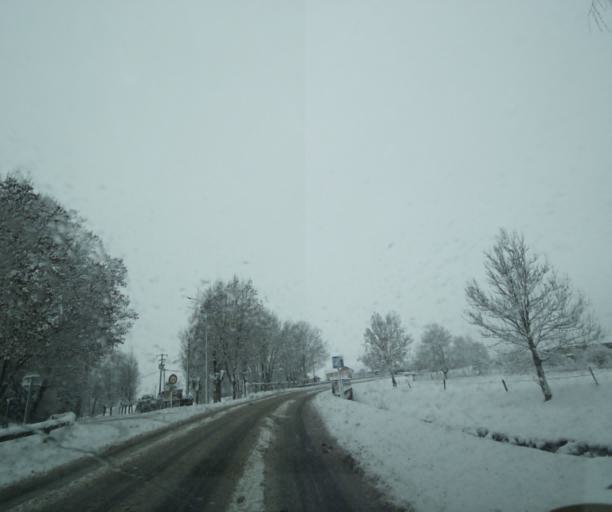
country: FR
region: Champagne-Ardenne
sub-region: Departement de la Haute-Marne
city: Saint-Dizier
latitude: 48.5847
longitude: 4.9018
